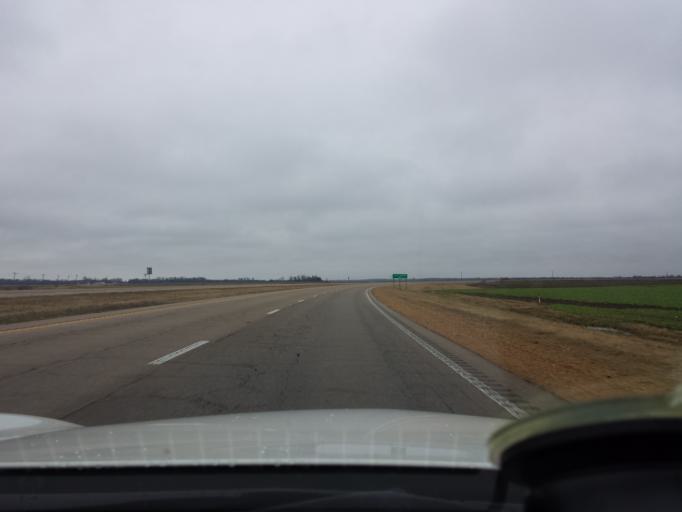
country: US
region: Mississippi
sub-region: Chickasaw County
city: Okolona
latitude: 33.9290
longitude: -88.7385
